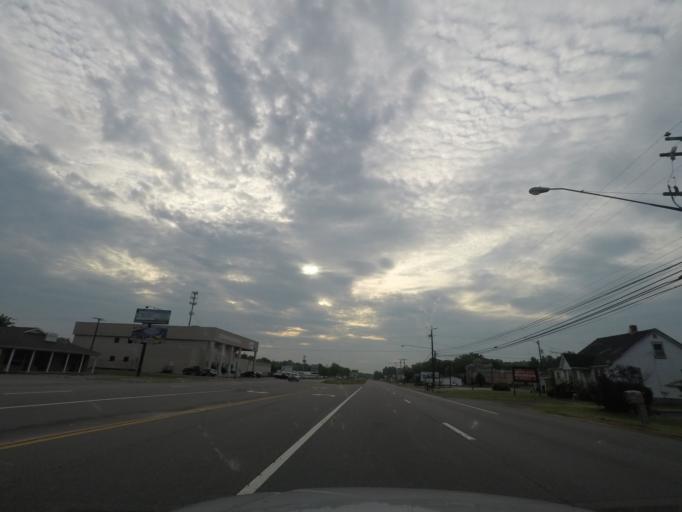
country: US
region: Virginia
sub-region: Halifax County
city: South Boston
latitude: 36.6878
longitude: -78.8971
